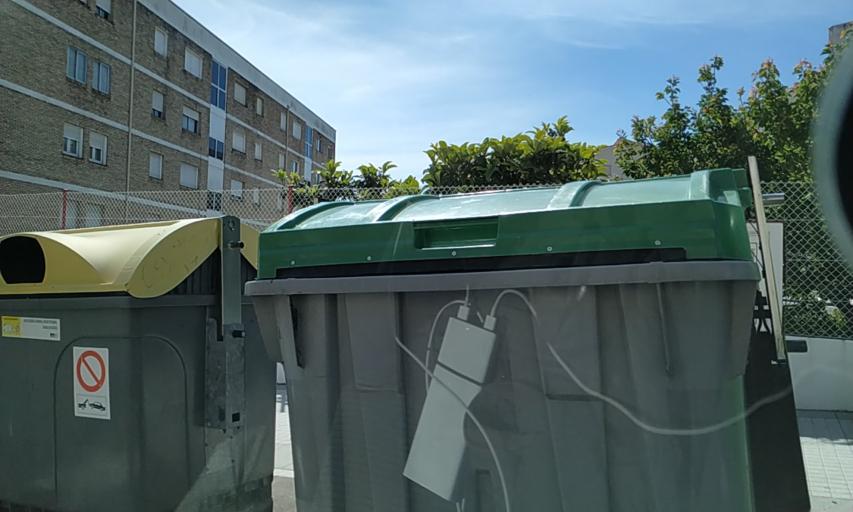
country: ES
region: Galicia
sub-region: Provincia de Pontevedra
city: Sanxenxo
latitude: 42.4064
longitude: -8.8125
